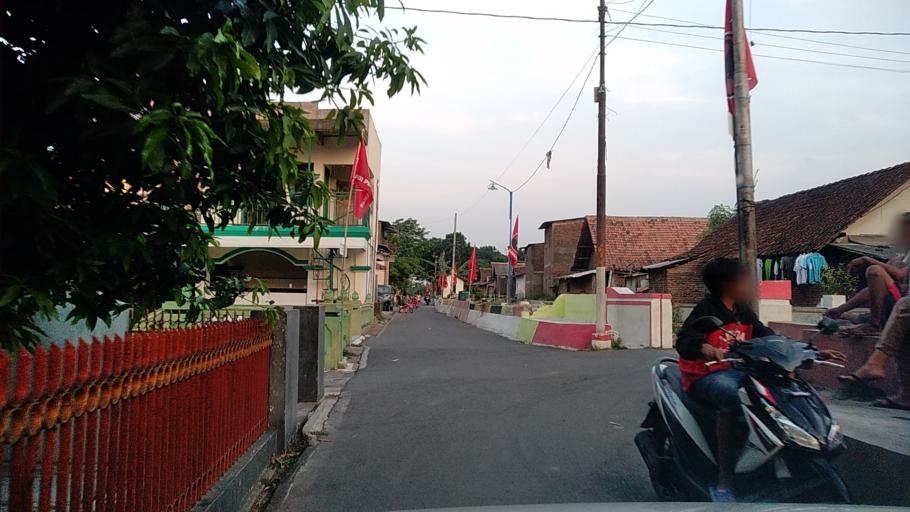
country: ID
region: Central Java
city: Semarang
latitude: -6.9718
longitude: 110.3129
